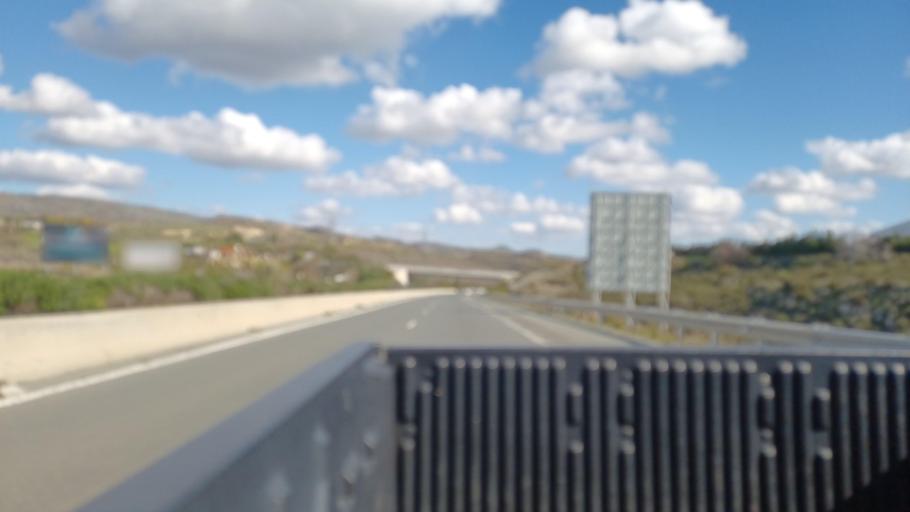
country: CY
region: Pafos
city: Mesogi
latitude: 34.7688
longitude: 32.4749
